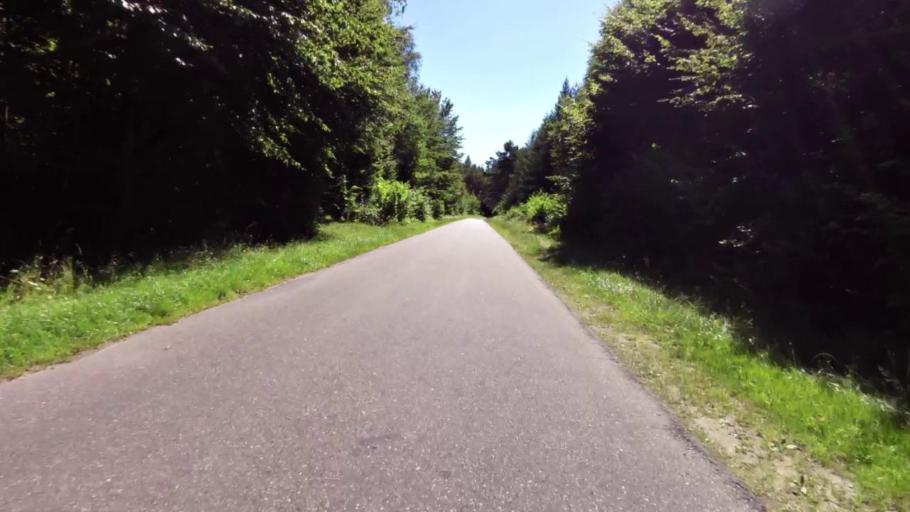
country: PL
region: West Pomeranian Voivodeship
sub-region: Powiat szczecinecki
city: Bialy Bor
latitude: 53.9412
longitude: 16.8535
